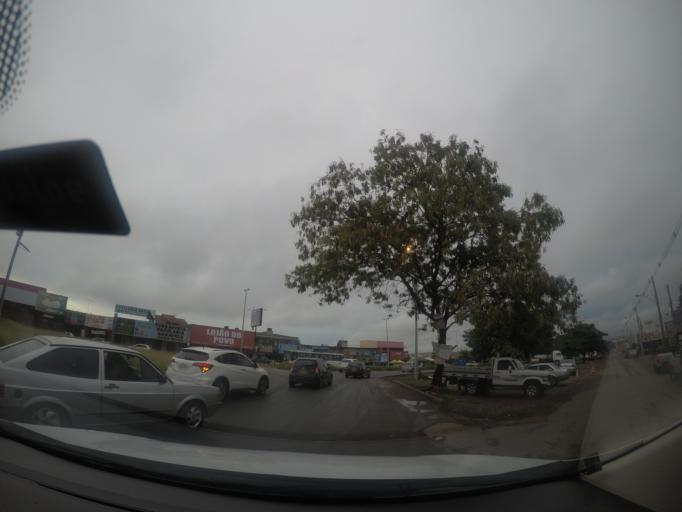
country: BR
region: Goias
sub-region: Aparecida De Goiania
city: Aparecida de Goiania
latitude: -16.7635
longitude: -49.3474
